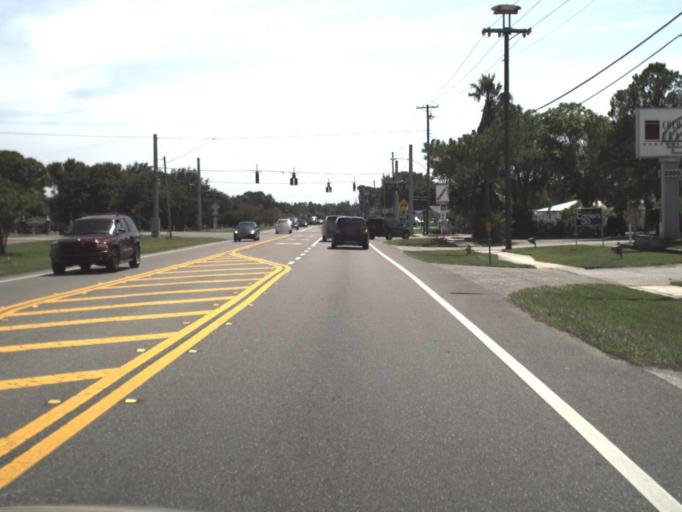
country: US
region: Florida
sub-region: Pinellas County
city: Dunedin
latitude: 28.0418
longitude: -82.7832
